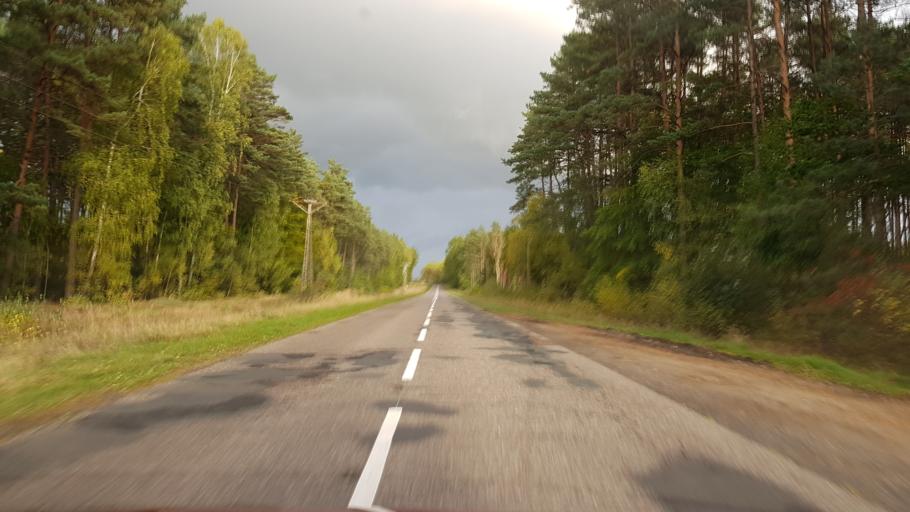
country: PL
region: West Pomeranian Voivodeship
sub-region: Powiat walecki
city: Walcz
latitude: 53.1797
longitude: 16.3548
